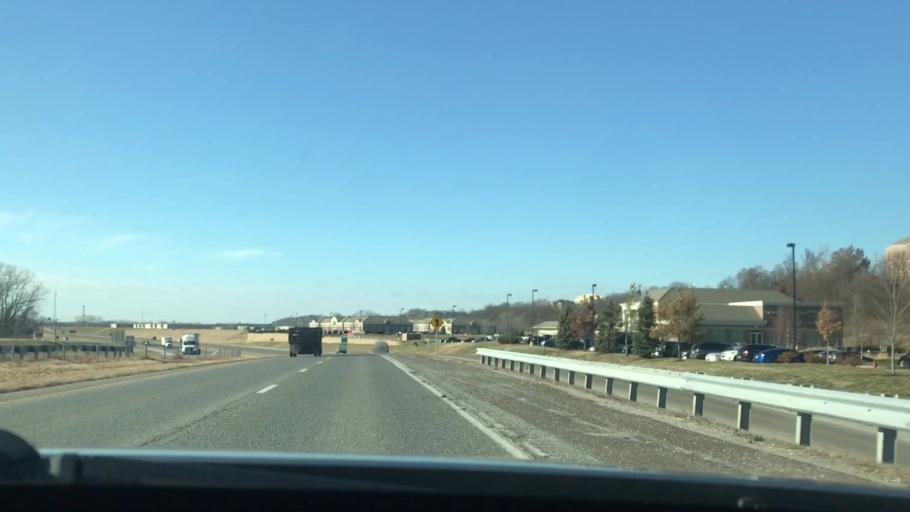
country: US
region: Missouri
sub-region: Platte County
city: Riverside
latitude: 39.1657
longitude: -94.5995
